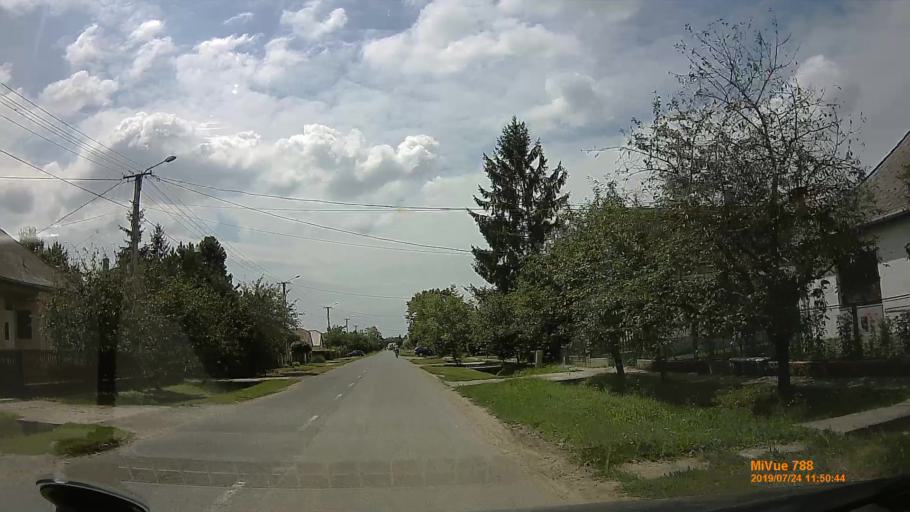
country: UA
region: Zakarpattia
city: Batiovo
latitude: 48.2388
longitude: 22.4358
